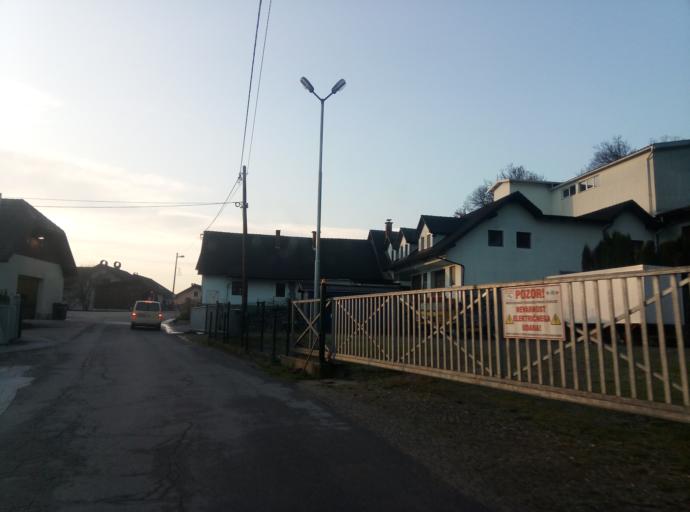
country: SI
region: Vodice
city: Vodice
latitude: 46.1744
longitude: 14.4831
